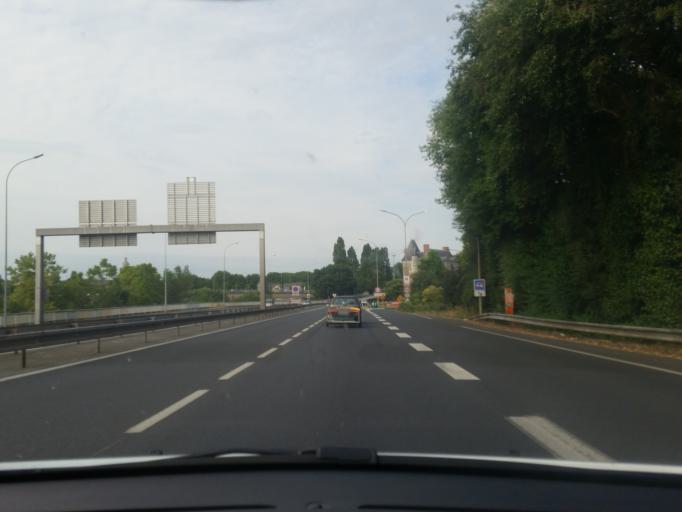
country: FR
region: Pays de la Loire
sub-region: Departement de Maine-et-Loire
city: Angers
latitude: 47.4681
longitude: -0.5654
